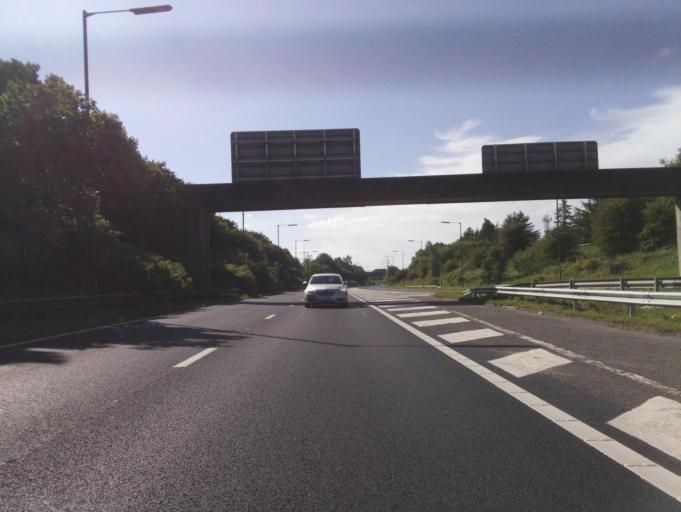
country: GB
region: England
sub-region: Borough of Bolton
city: Kearsley
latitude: 53.5329
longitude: -2.3837
